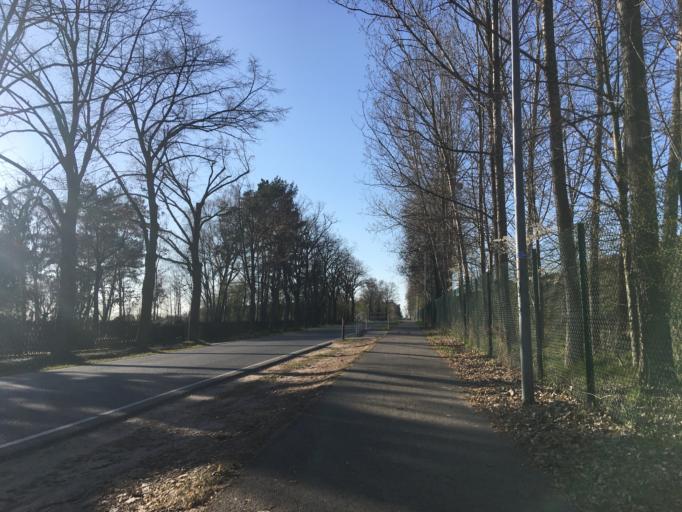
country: DE
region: Berlin
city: Buch
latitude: 52.6324
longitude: 13.5402
